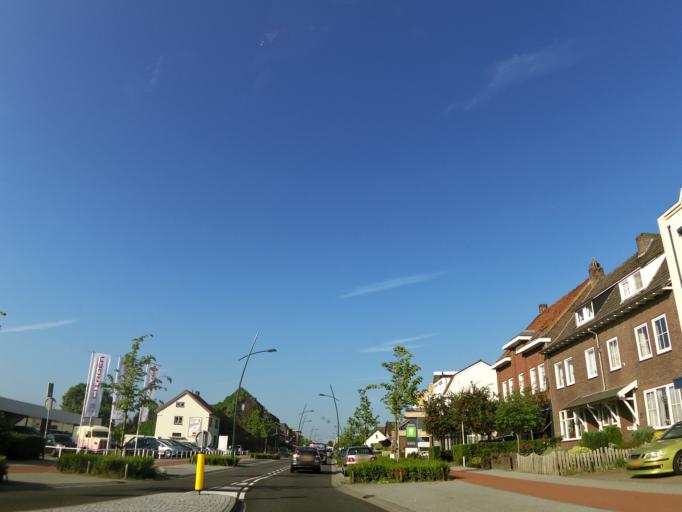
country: NL
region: Limburg
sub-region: Gemeente Beek
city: Beek
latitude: 50.9449
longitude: 5.7994
